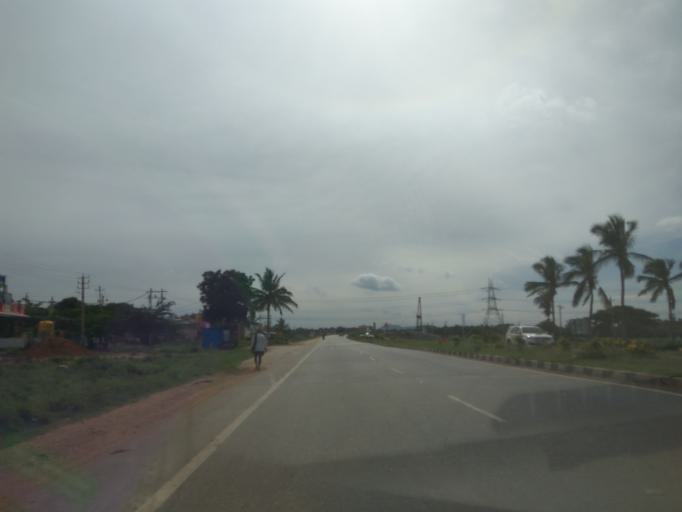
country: IN
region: Karnataka
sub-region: Bangalore Rural
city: Dasarahalli
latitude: 13.1338
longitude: 77.9457
